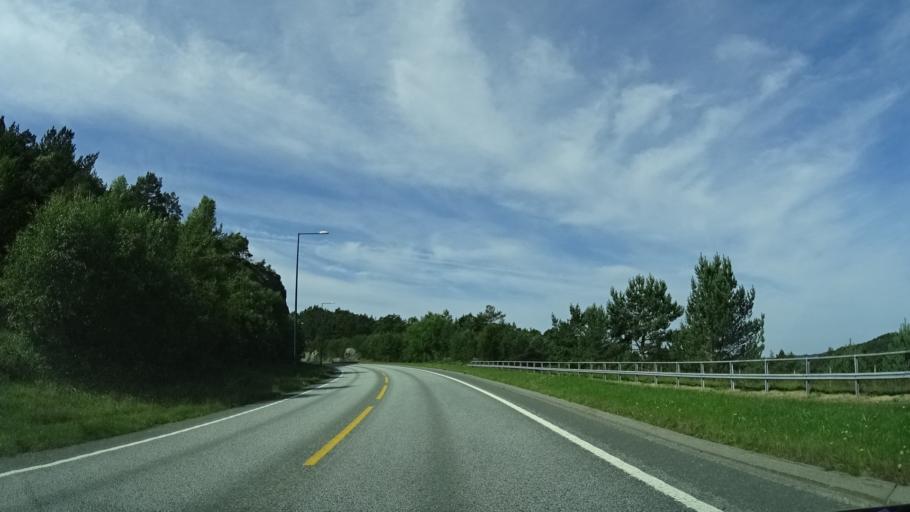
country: NO
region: Hordaland
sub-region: Stord
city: Sagvag
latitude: 59.7608
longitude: 5.4137
